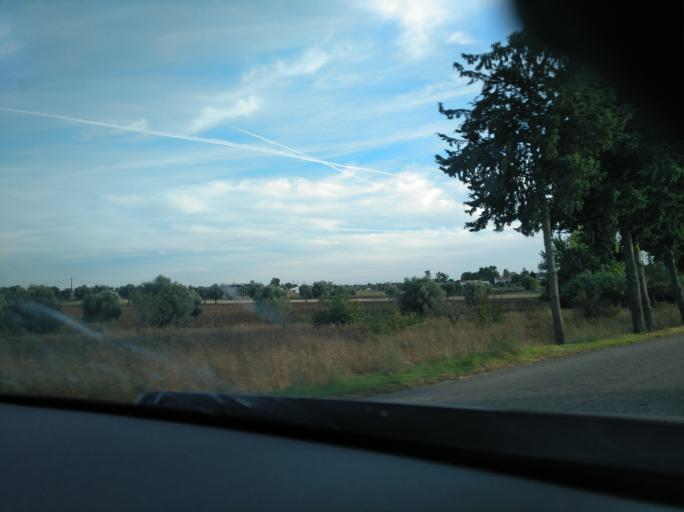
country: PT
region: Evora
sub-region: Arraiolos
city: Arraiolos
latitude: 38.8348
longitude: -7.8325
